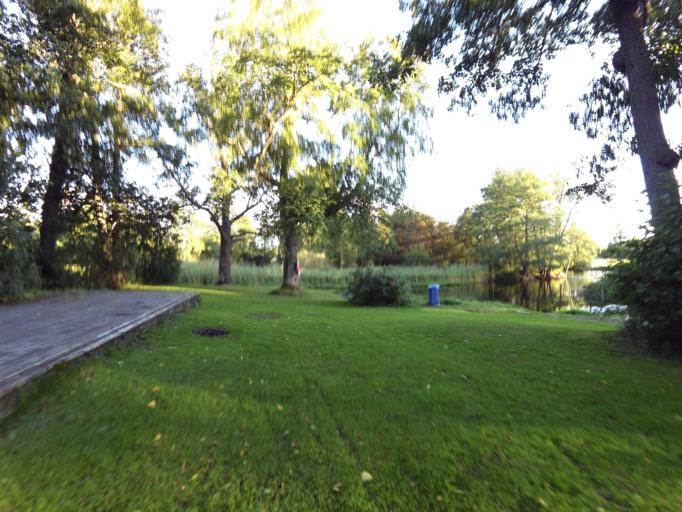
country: SE
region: Gaevleborg
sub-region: Gavle Kommun
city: Gavle
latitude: 60.7172
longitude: 17.1424
